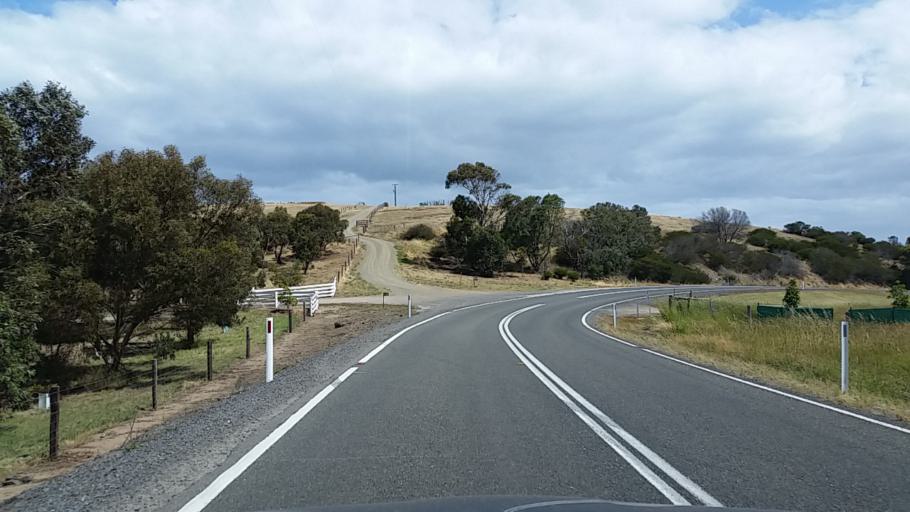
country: AU
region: South Australia
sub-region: Alexandrina
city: Port Elliot
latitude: -35.5042
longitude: 138.6711
